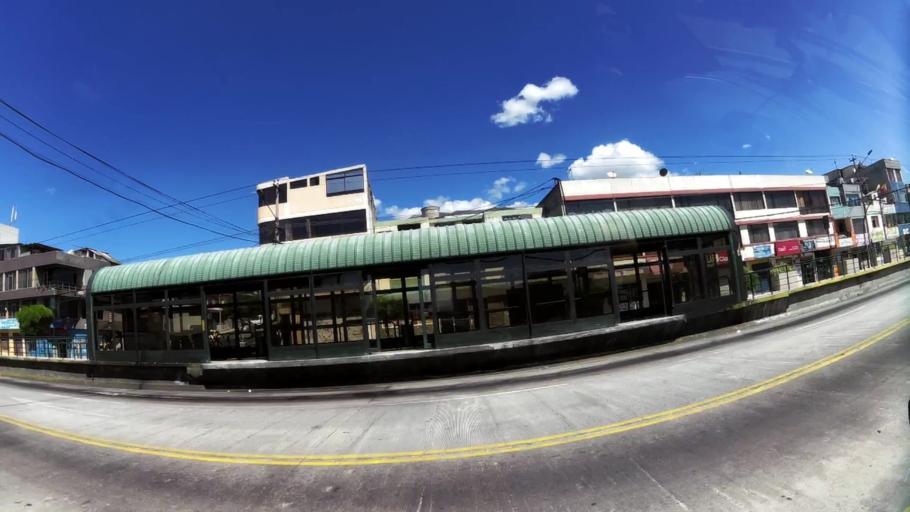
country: EC
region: Pichincha
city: Quito
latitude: -0.1583
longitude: -78.4879
